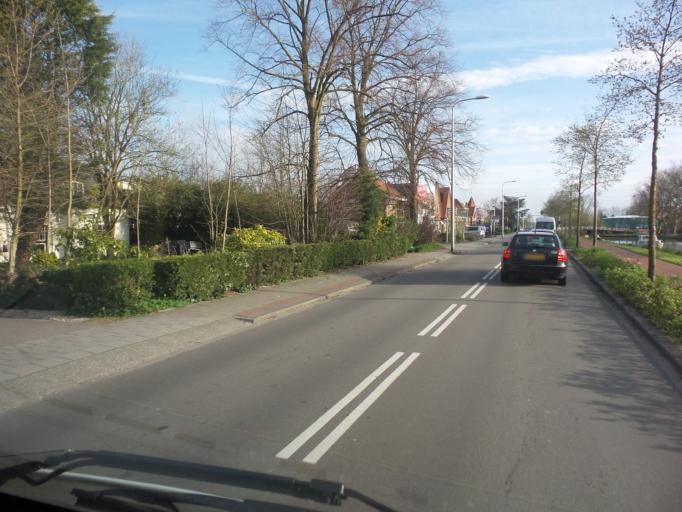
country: NL
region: South Holland
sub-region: Bodegraven-Reeuwijk
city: Reeuwijk
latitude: 52.0410
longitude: 4.7209
